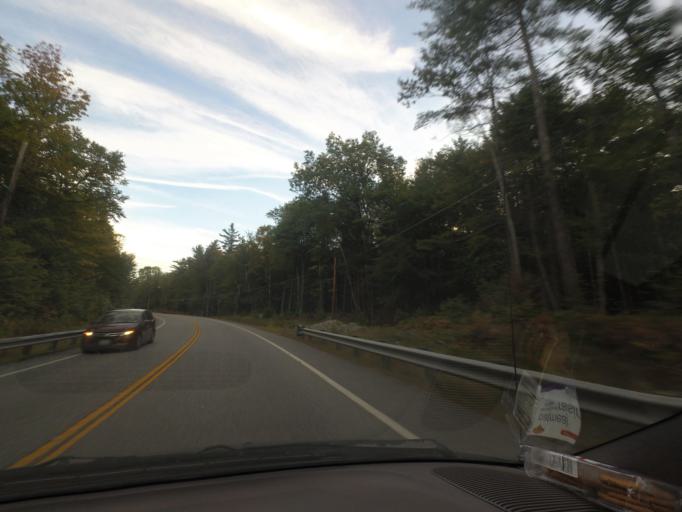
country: US
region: New Hampshire
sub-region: Cheshire County
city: Harrisville
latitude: 43.0669
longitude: -72.0663
